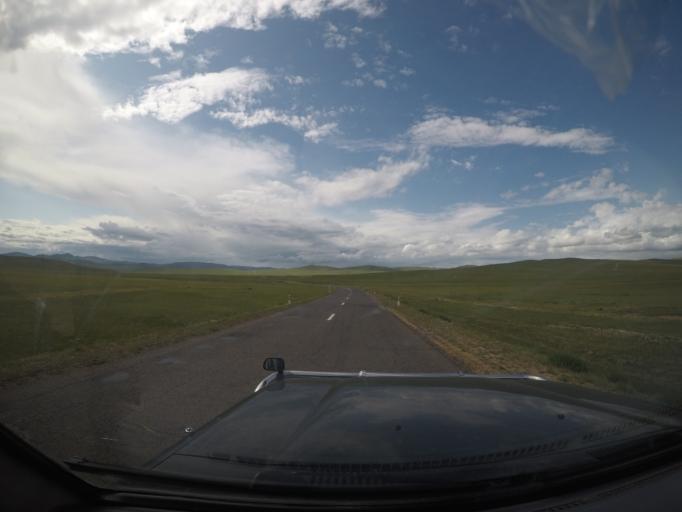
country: MN
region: Hentiy
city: Modot
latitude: 47.5941
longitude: 109.2542
